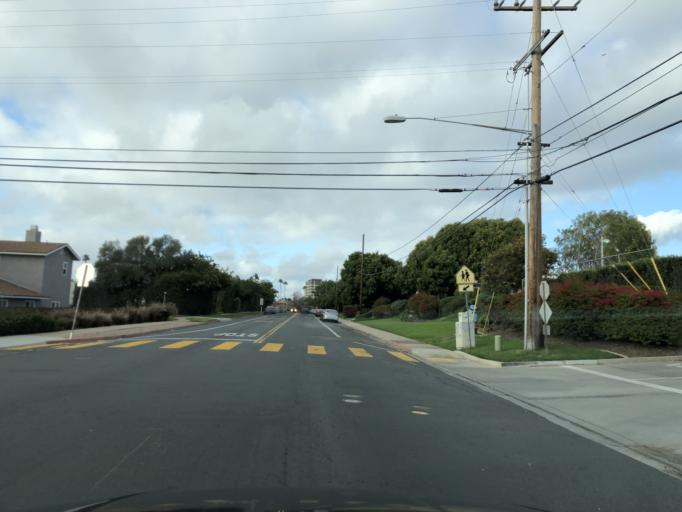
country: US
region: California
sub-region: San Diego County
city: La Jolla
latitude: 32.8138
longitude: -117.1820
